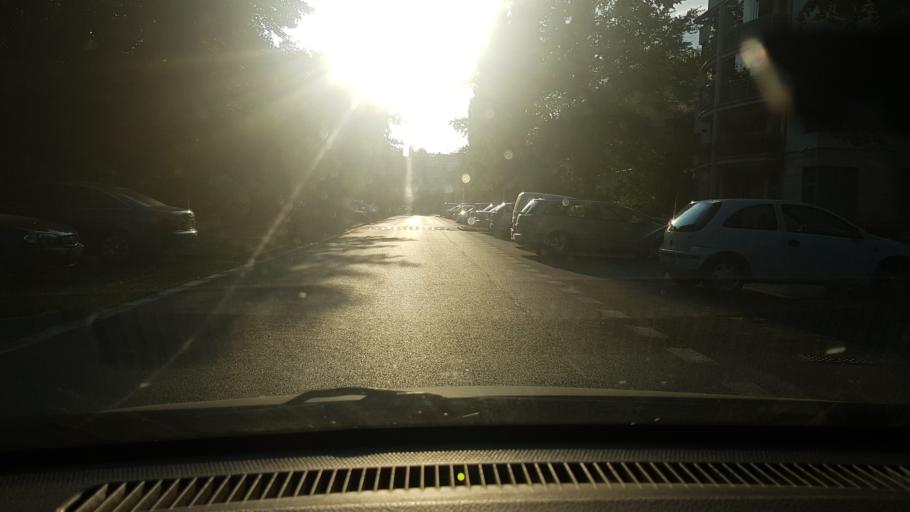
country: PL
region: Masovian Voivodeship
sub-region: Warszawa
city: Wola
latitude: 52.2432
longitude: 20.9503
